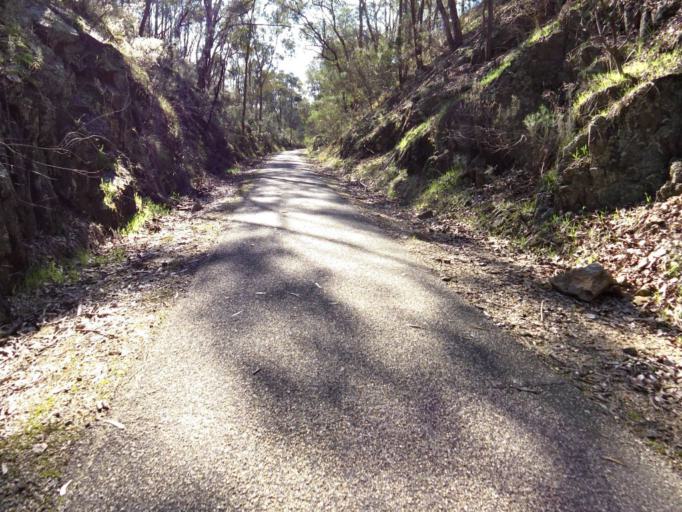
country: AU
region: Victoria
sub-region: Wangaratta
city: Wangaratta
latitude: -36.4083
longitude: 146.6167
